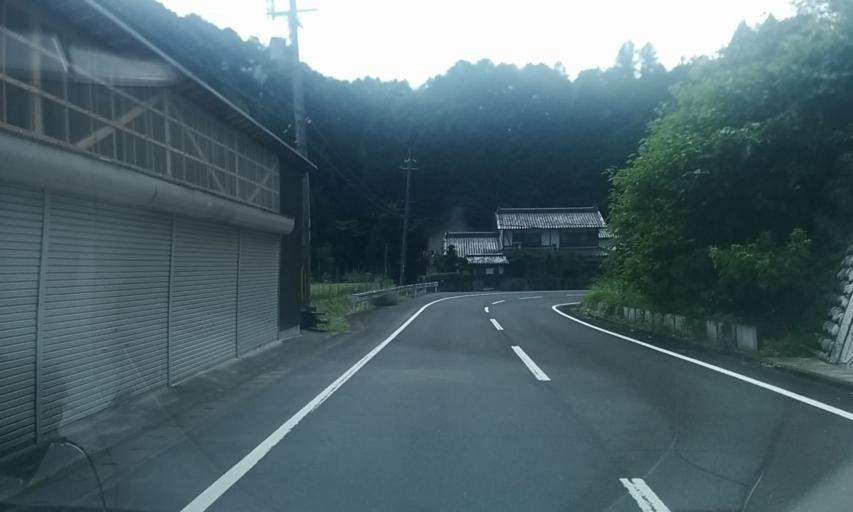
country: JP
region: Kyoto
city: Fukuchiyama
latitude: 35.3674
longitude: 135.1638
